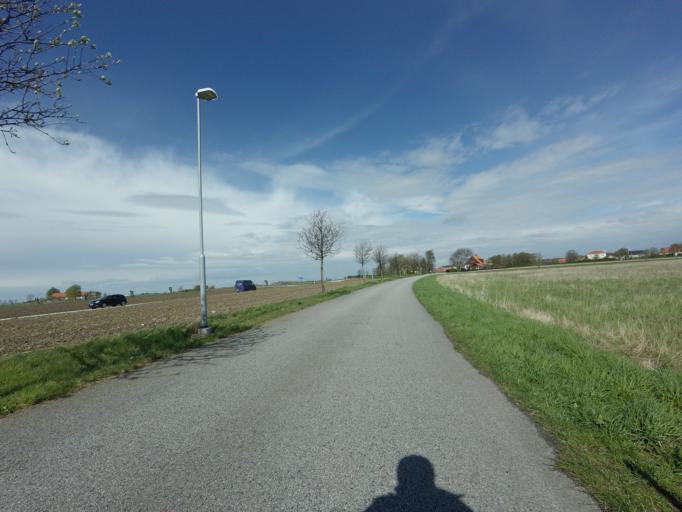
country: SE
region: Skane
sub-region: Vellinge Kommun
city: Vellinge
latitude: 55.4903
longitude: 13.0063
